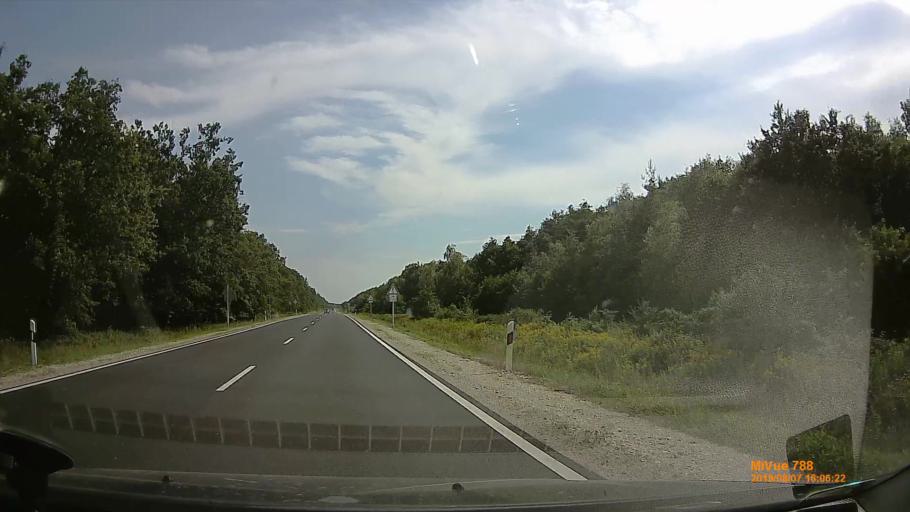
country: HU
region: Vas
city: Kormend
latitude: 46.9388
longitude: 16.6013
